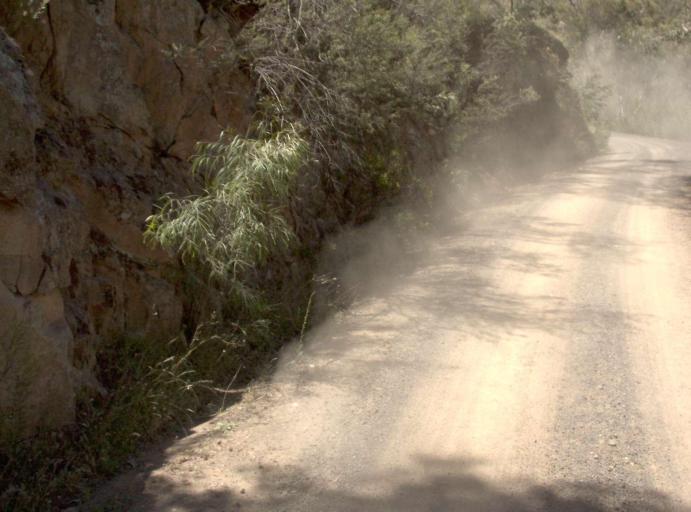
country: AU
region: New South Wales
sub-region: Snowy River
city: Jindabyne
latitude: -37.0739
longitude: 148.4654
